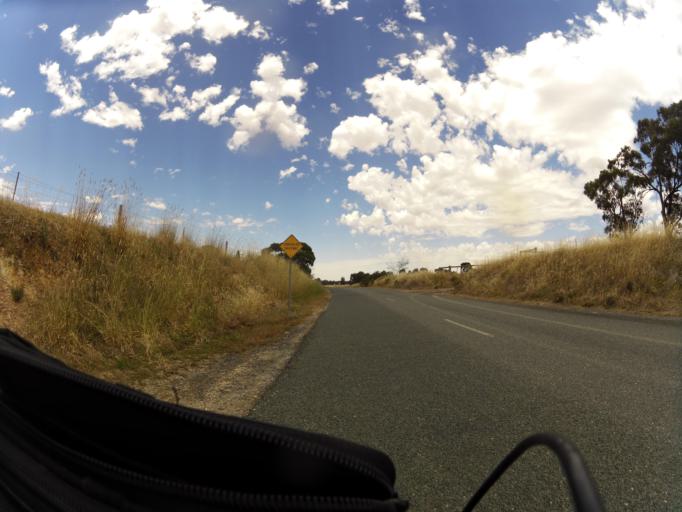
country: AU
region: Victoria
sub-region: Greater Shepparton
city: Shepparton
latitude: -36.6314
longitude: 145.2107
